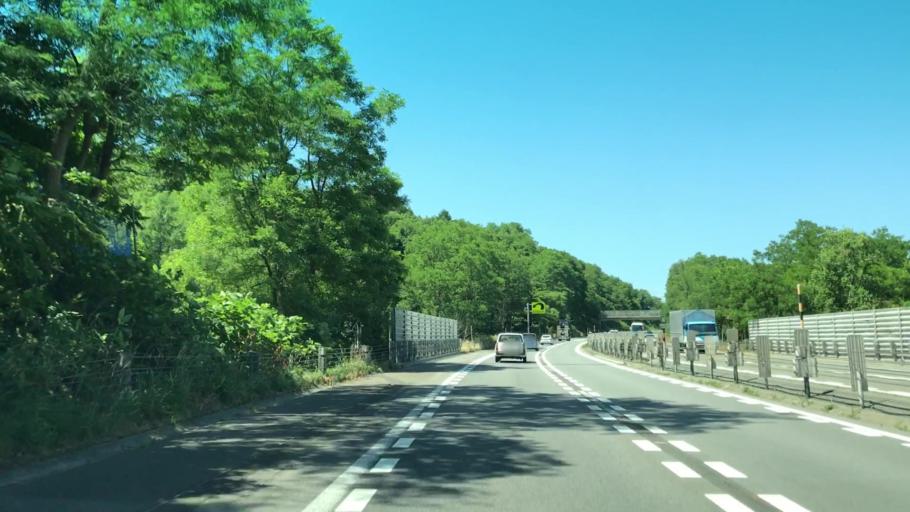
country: JP
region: Hokkaido
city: Otaru
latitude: 43.1469
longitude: 141.1332
